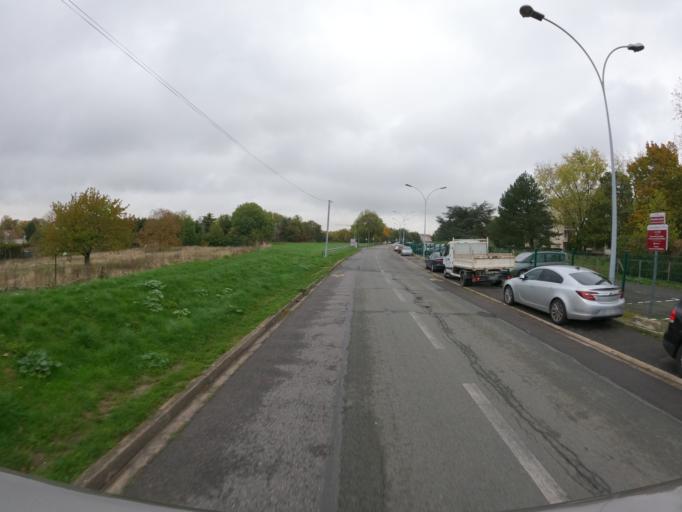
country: FR
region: Ile-de-France
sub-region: Departement du Val-de-Marne
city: Chennevieres-sur-Marne
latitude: 48.7894
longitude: 2.5286
